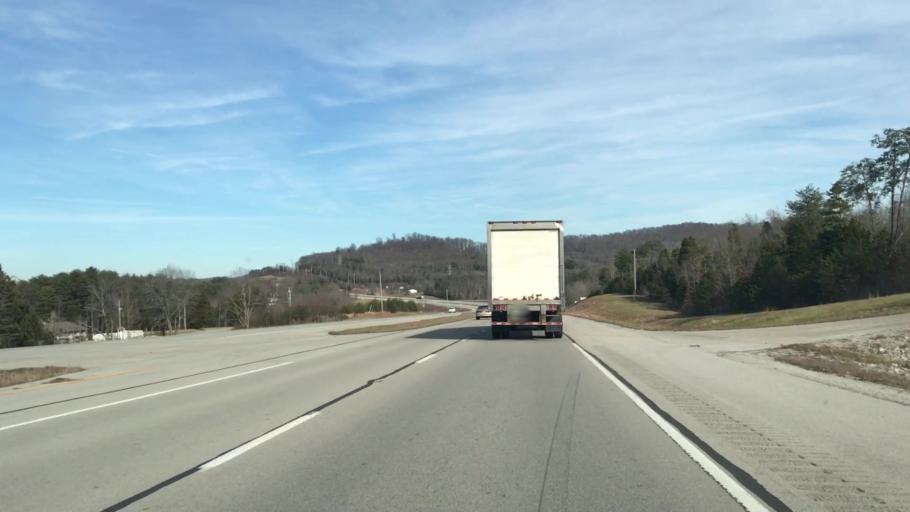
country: US
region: Kentucky
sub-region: Pulaski County
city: Somerset
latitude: 37.0177
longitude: -84.5980
